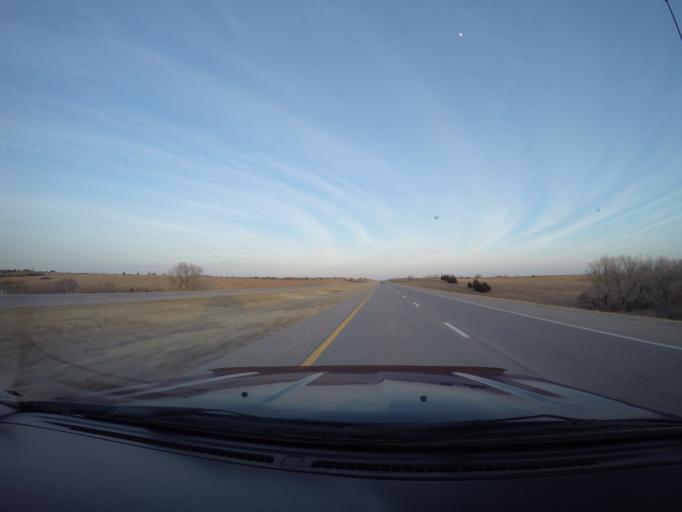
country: US
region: Kansas
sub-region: Saline County
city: Salina
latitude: 38.9068
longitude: -97.5148
